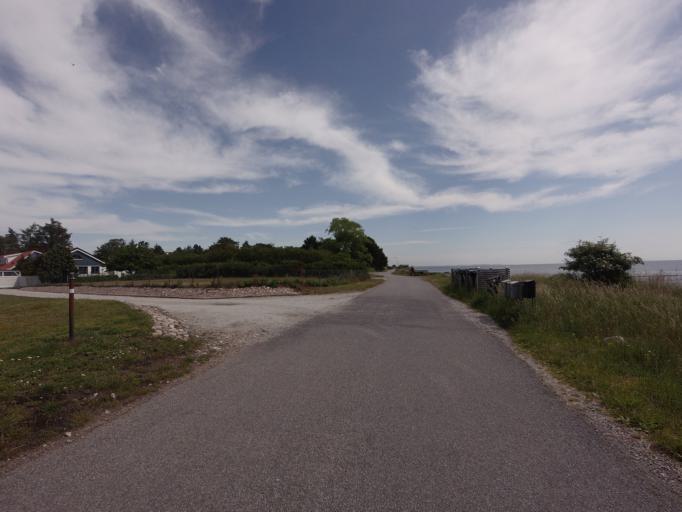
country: SE
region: Skane
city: Smygehamn
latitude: 55.3543
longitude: 13.4218
